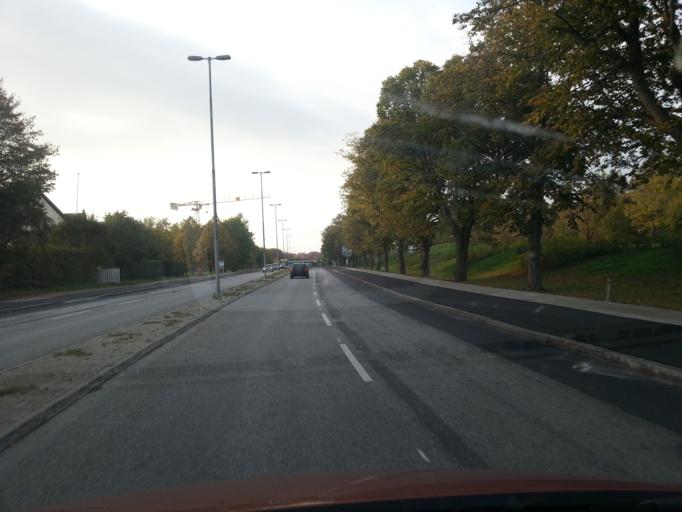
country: SE
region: Skane
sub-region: Lunds Kommun
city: Lund
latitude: 55.6956
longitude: 13.1867
